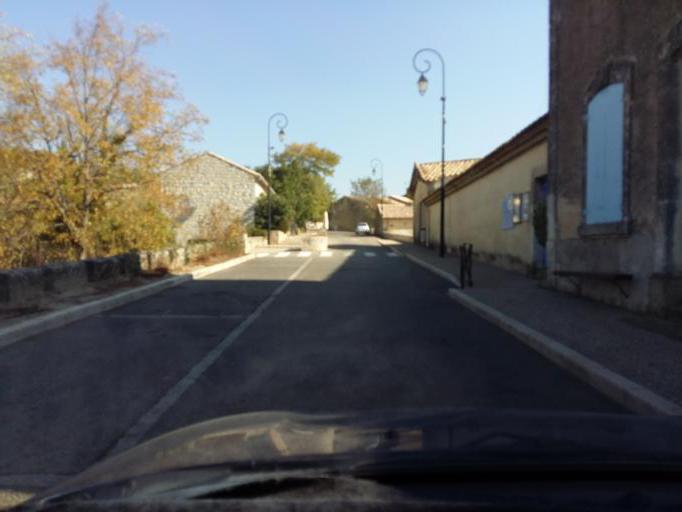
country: FR
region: Rhone-Alpes
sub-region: Departement de la Drome
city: Rochegude
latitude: 44.2277
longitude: 4.8503
